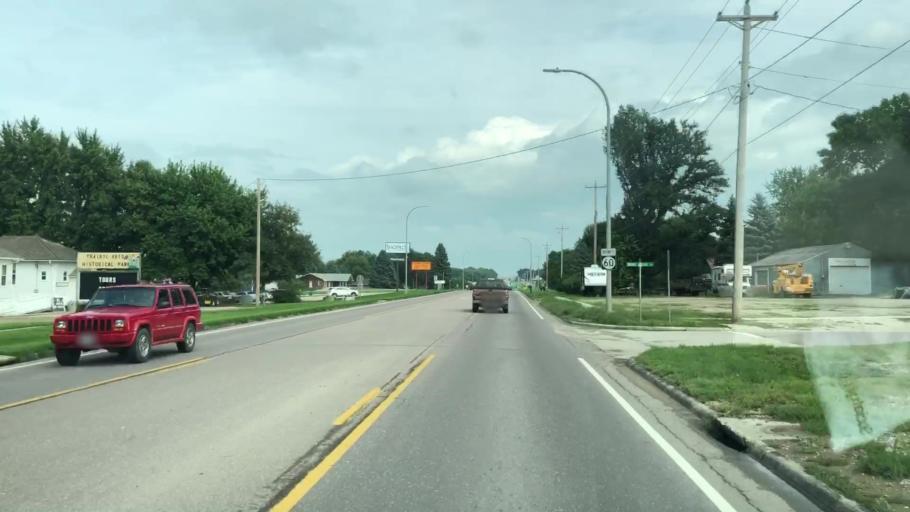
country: US
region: Iowa
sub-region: O'Brien County
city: Sheldon
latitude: 43.1860
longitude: -95.8412
